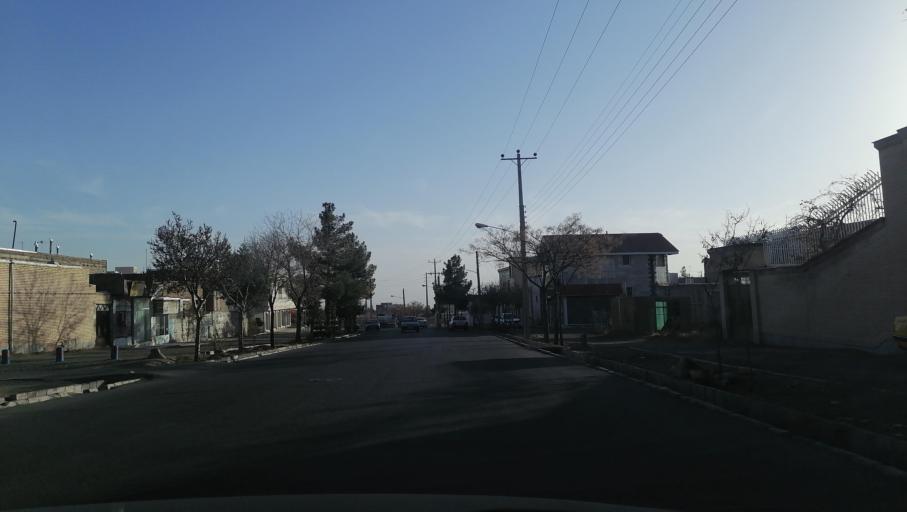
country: IR
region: Razavi Khorasan
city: Sabzevar
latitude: 36.2884
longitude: 57.6762
